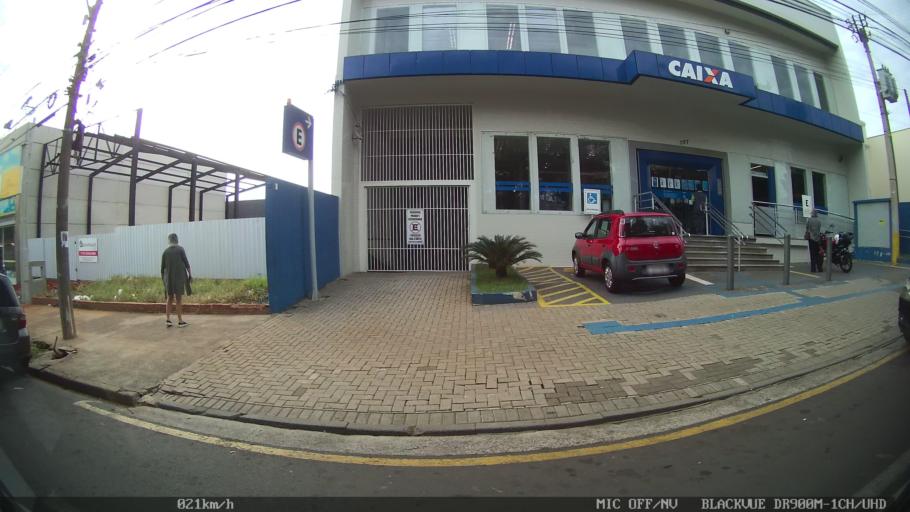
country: BR
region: Sao Paulo
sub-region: Piracicaba
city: Piracicaba
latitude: -22.7388
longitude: -47.6266
